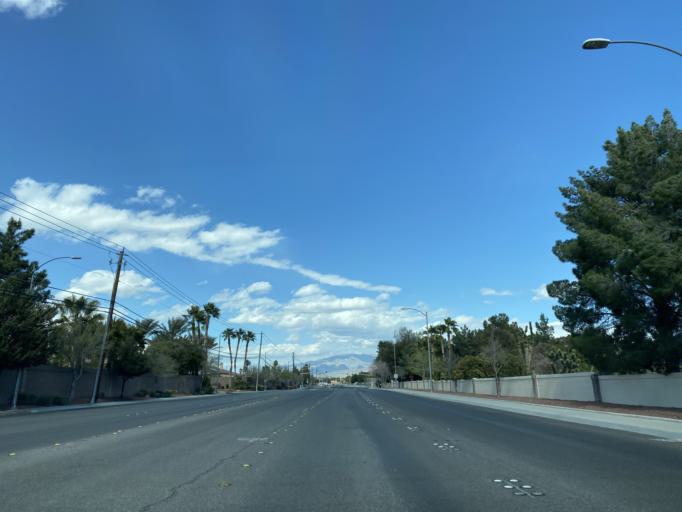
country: US
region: Nevada
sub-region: Clark County
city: Spring Valley
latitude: 36.2455
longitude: -115.2603
